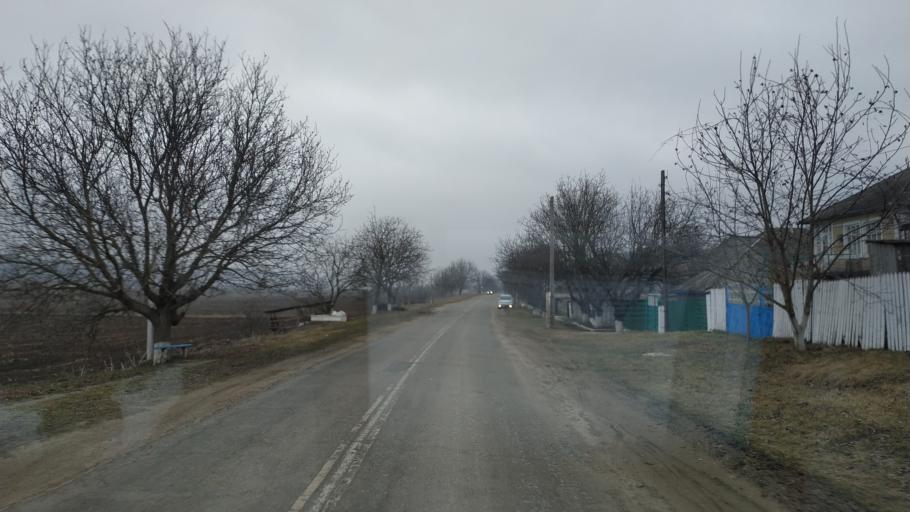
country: MD
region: Hincesti
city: Hincesti
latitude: 46.9638
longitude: 28.4829
